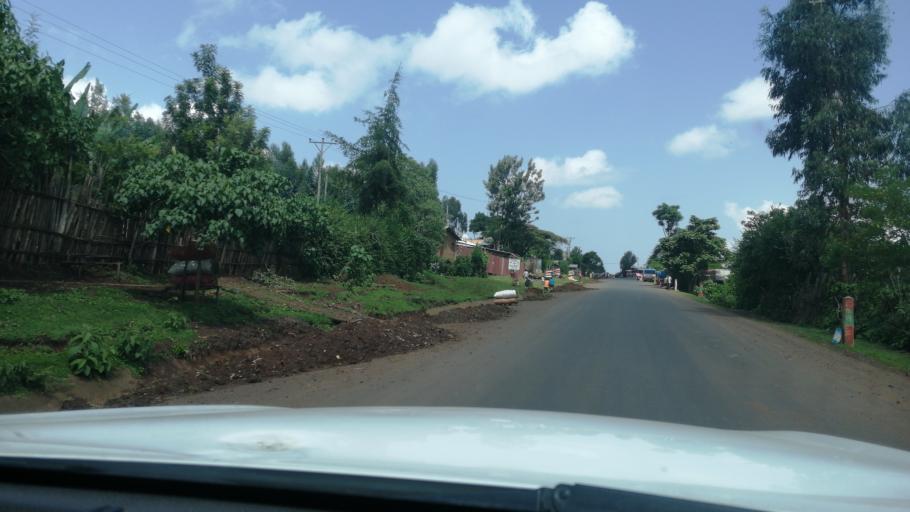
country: ET
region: Oromiya
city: Gedo
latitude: 8.9821
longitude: 37.5960
